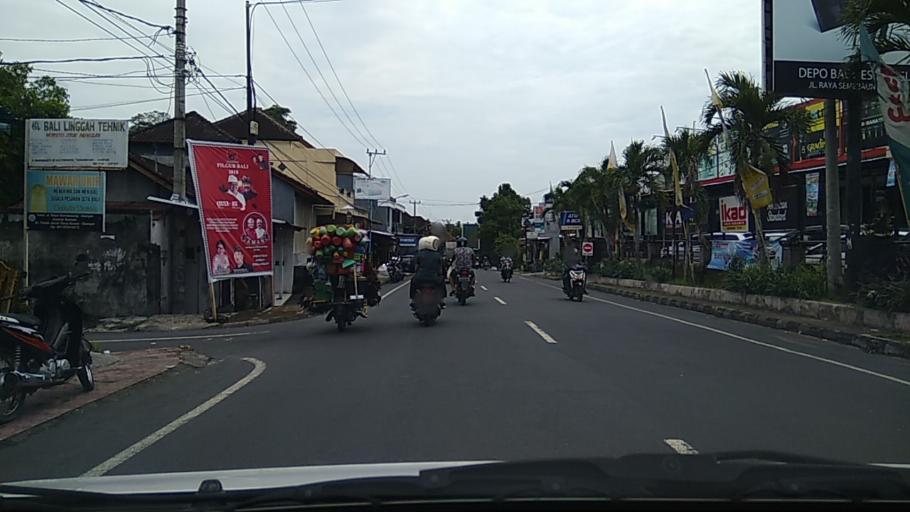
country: ID
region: Bali
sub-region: Kabupaten Gianyar
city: Ubud
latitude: -8.5350
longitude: 115.3081
